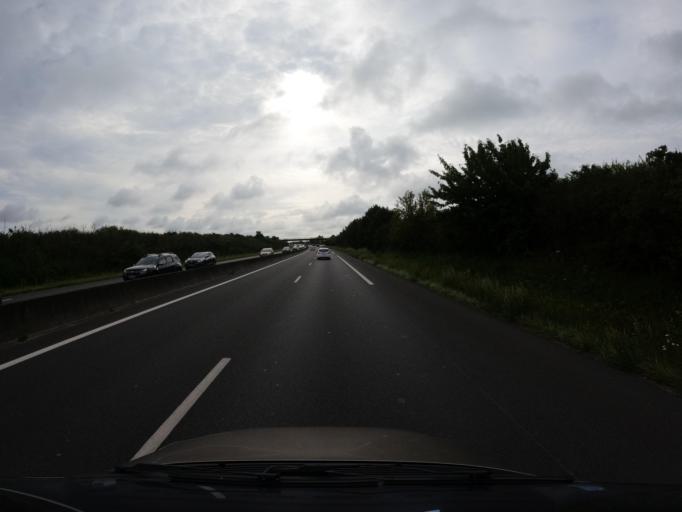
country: FR
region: Centre
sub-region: Departement d'Indre-et-Loire
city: Villandry
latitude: 47.3020
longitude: 0.5329
